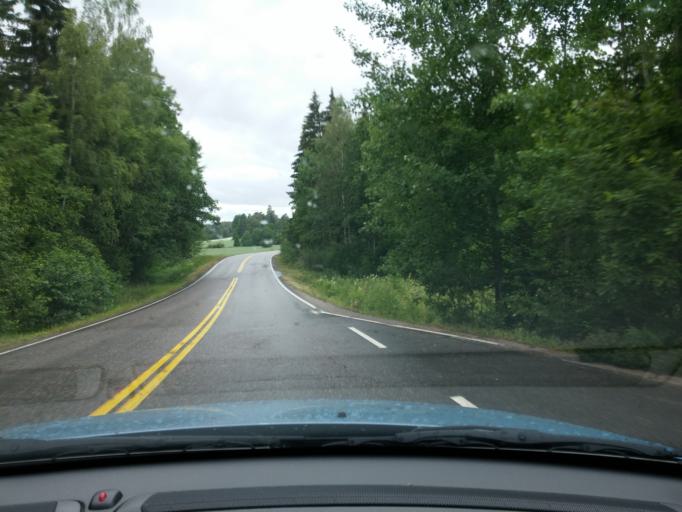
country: FI
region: Uusimaa
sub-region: Porvoo
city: Askola
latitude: 60.5510
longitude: 25.6661
